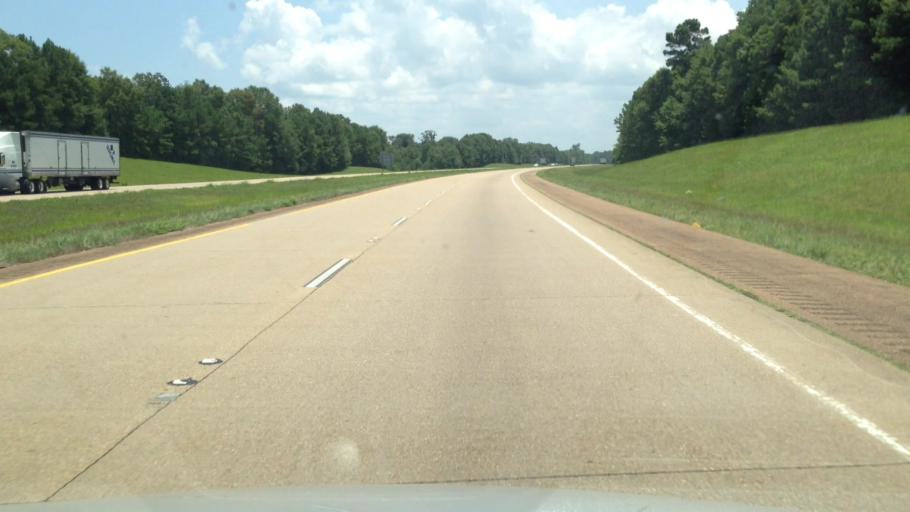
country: US
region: Louisiana
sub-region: Rapides Parish
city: Woodworth
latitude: 31.1550
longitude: -92.4548
